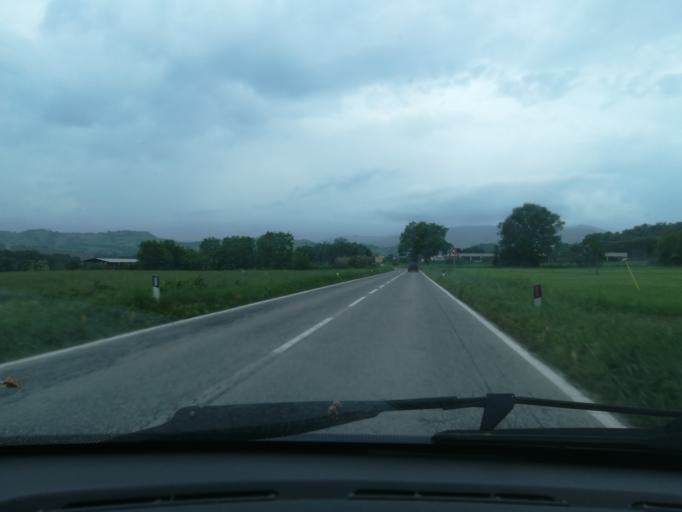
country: IT
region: The Marches
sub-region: Provincia di Macerata
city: San Severino Marche
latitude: 43.2553
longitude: 13.2328
